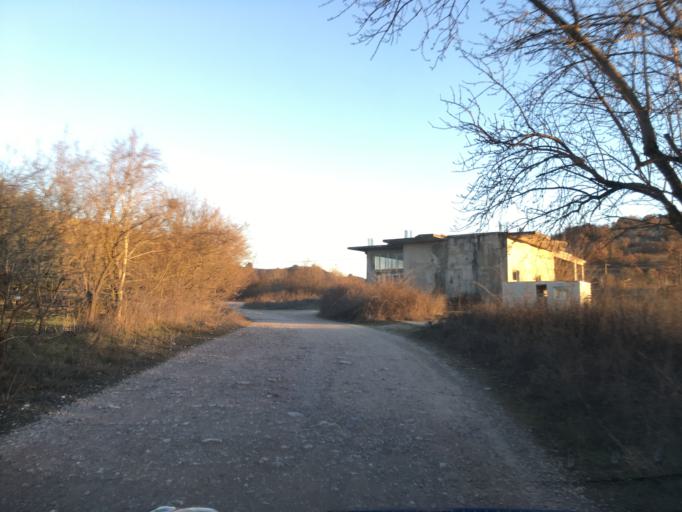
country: GR
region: West Macedonia
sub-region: Nomos Kozanis
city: Koila
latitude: 40.3299
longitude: 21.8097
